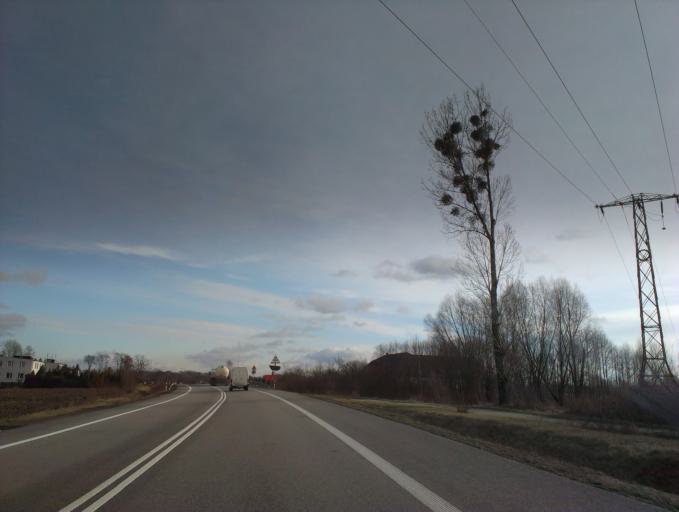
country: PL
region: Kujawsko-Pomorskie
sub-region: Powiat lipnowski
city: Kikol
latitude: 52.9187
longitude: 19.0994
